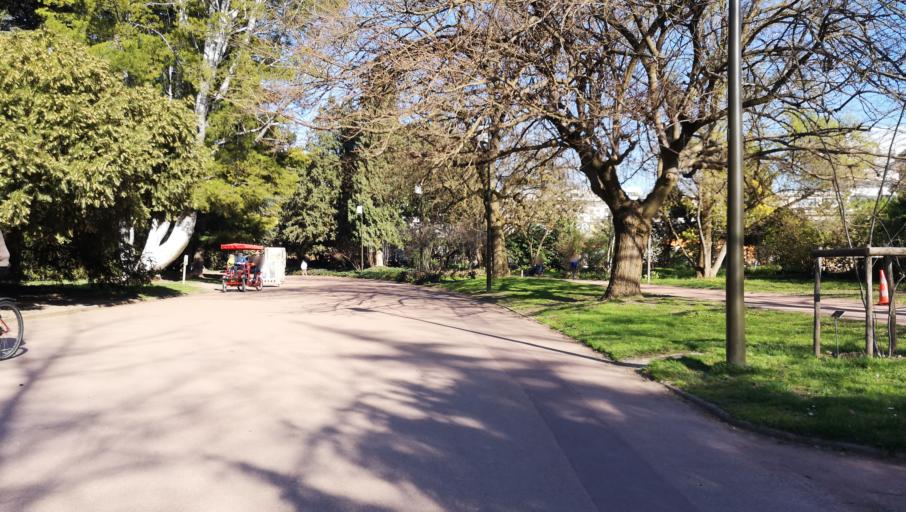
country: FR
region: Rhone-Alpes
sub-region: Departement du Rhone
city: Caluire-et-Cuire
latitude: 45.7739
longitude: 4.8568
